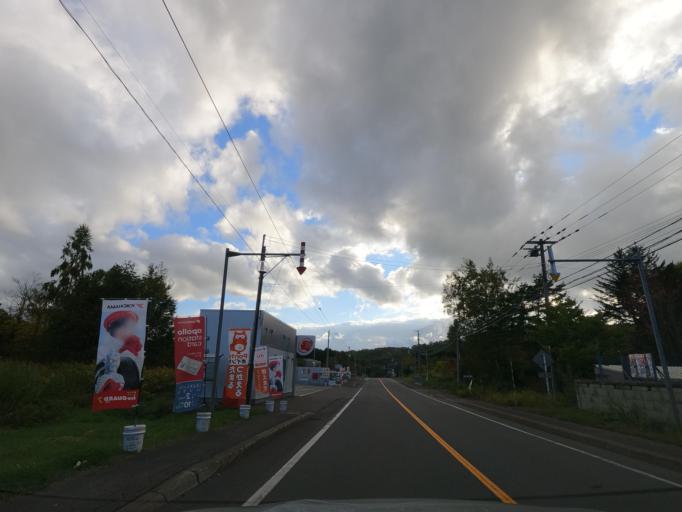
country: JP
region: Hokkaido
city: Date
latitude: 42.6690
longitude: 141.0775
